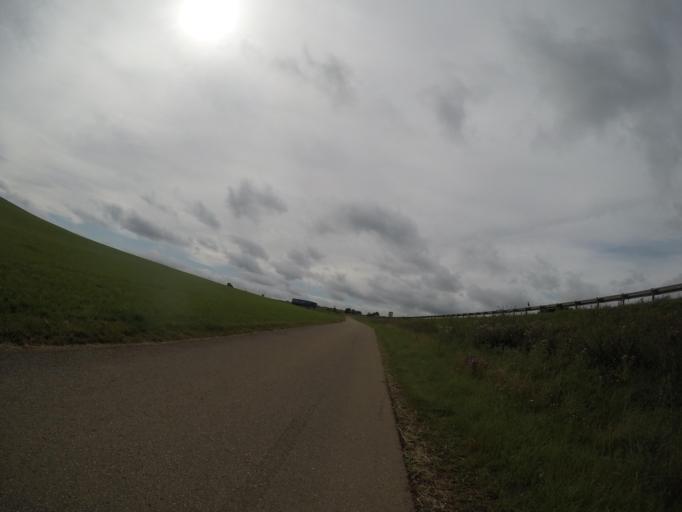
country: DE
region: Baden-Wuerttemberg
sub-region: Tuebingen Region
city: Laichingen
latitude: 48.4547
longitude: 9.6633
